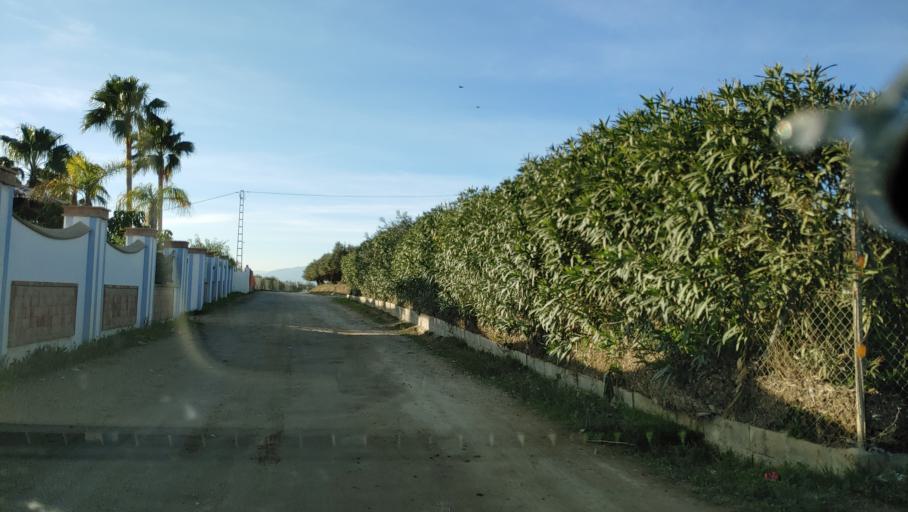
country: ES
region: Andalusia
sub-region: Provincia de Malaga
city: Cartama
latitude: 36.6861
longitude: -4.6468
